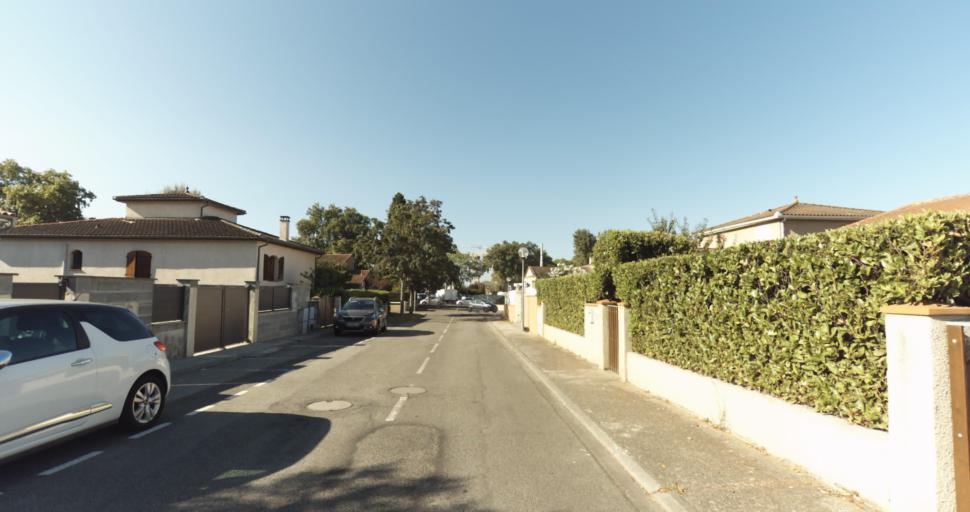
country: FR
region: Midi-Pyrenees
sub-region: Departement de la Haute-Garonne
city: L'Union
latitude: 43.6602
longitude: 1.4872
